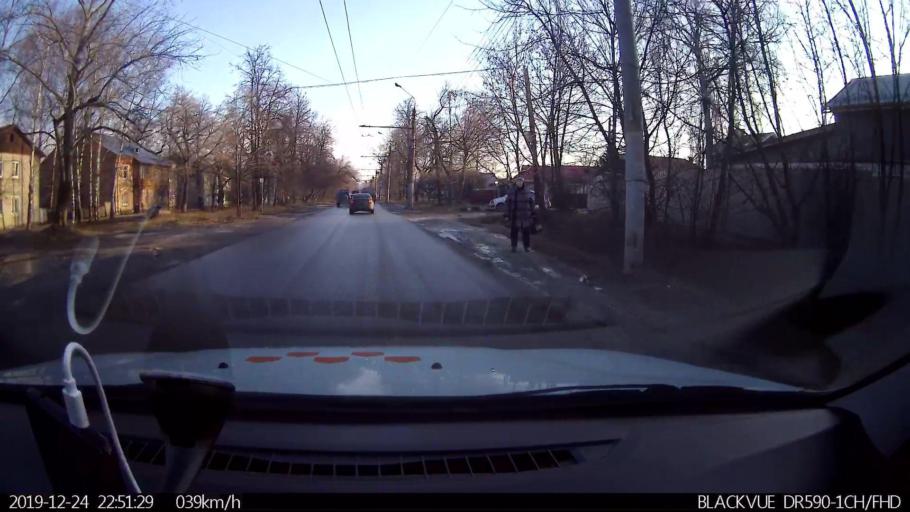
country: RU
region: Nizjnij Novgorod
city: Nizhniy Novgorod
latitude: 56.2880
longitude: 43.9105
